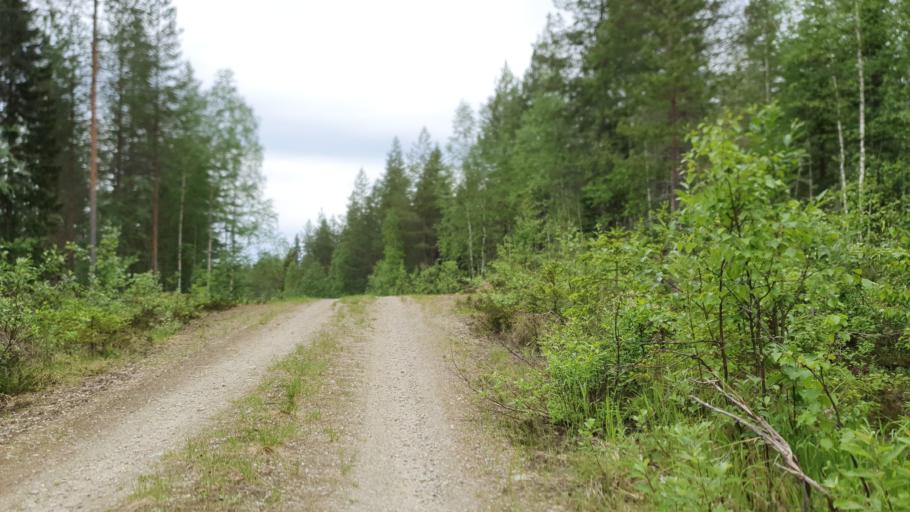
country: FI
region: Kainuu
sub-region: Kehys-Kainuu
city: Kuhmo
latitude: 64.4415
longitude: 29.6964
